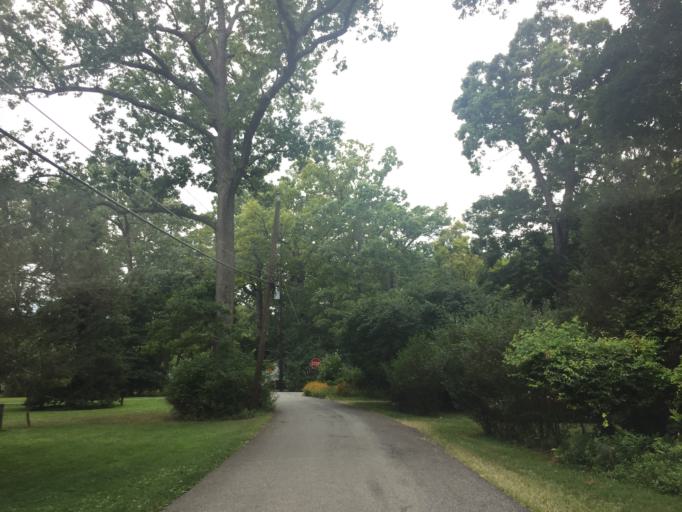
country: US
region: Maryland
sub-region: Montgomery County
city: Derwood
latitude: 39.1404
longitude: -77.1746
